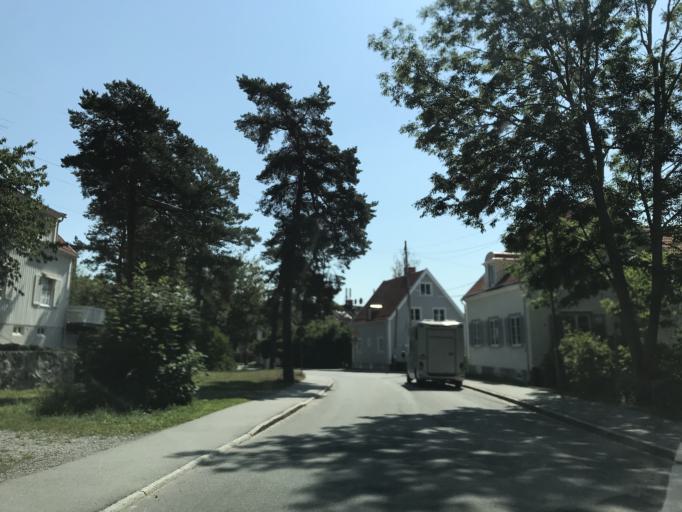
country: SE
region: Stockholm
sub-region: Stockholms Kommun
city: Bromma
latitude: 59.3256
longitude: 17.9556
